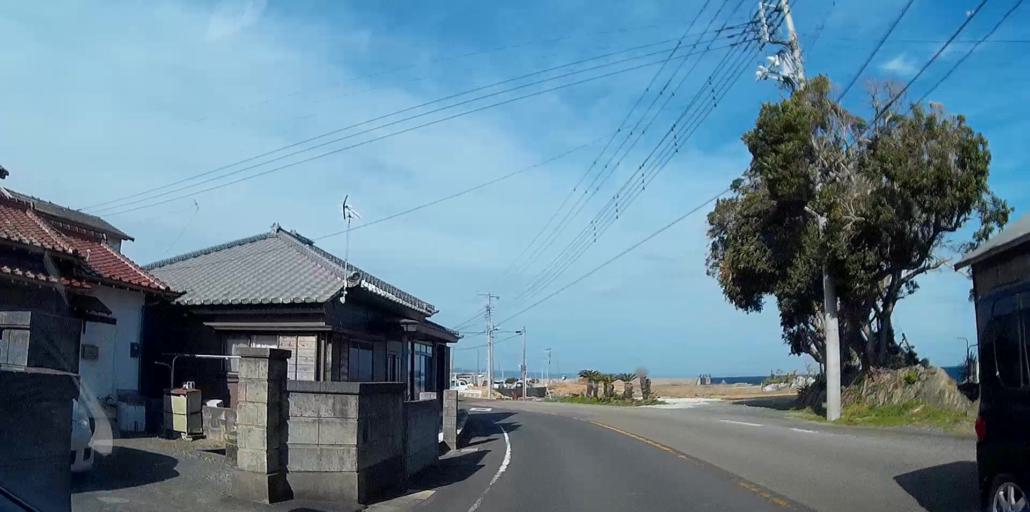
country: JP
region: Chiba
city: Tateyama
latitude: 34.9508
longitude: 139.9640
